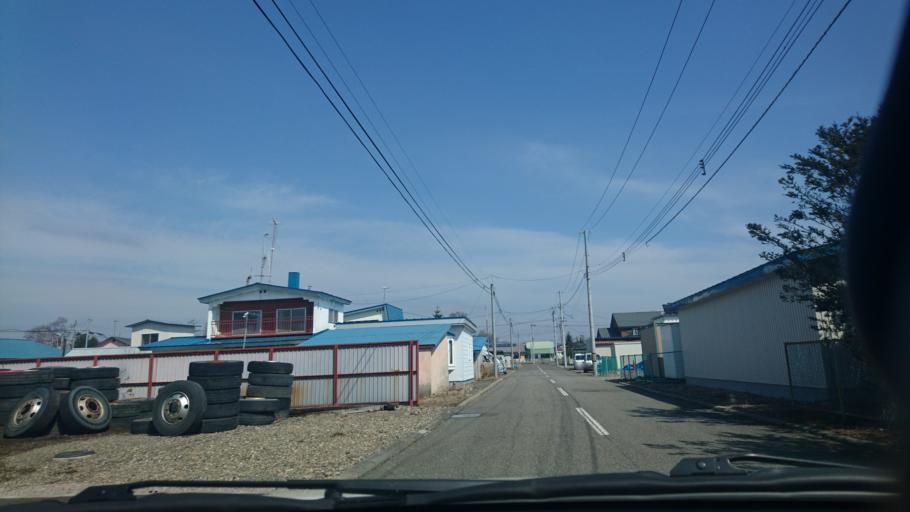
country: JP
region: Hokkaido
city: Otofuke
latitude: 43.0978
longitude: 143.2288
